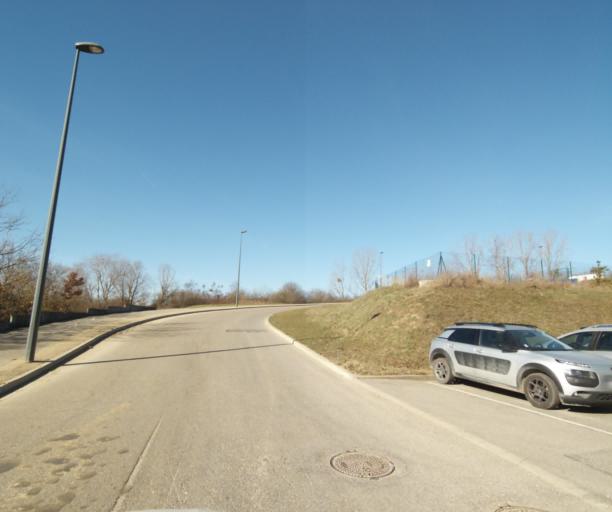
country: FR
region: Lorraine
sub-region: Departement de Meurthe-et-Moselle
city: Ludres
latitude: 48.6184
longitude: 6.1823
